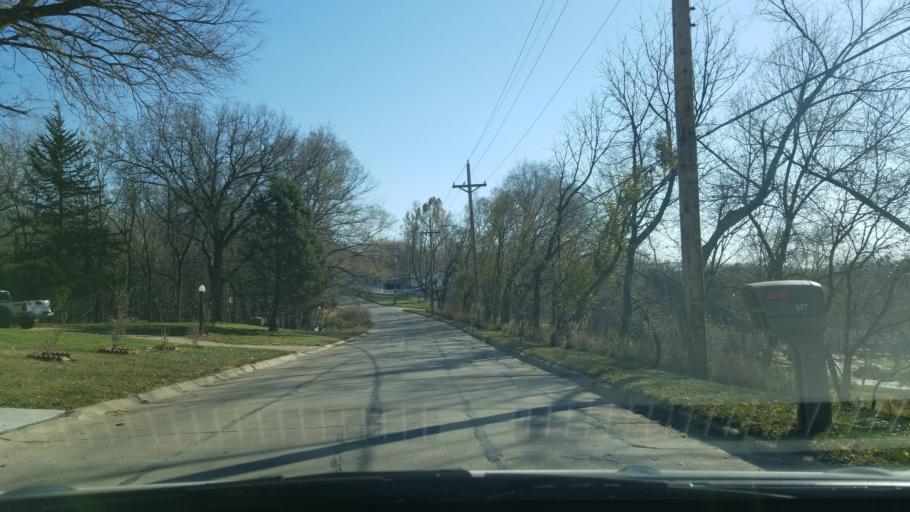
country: US
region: Nebraska
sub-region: Sarpy County
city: Bellevue
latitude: 41.1559
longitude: -95.9012
